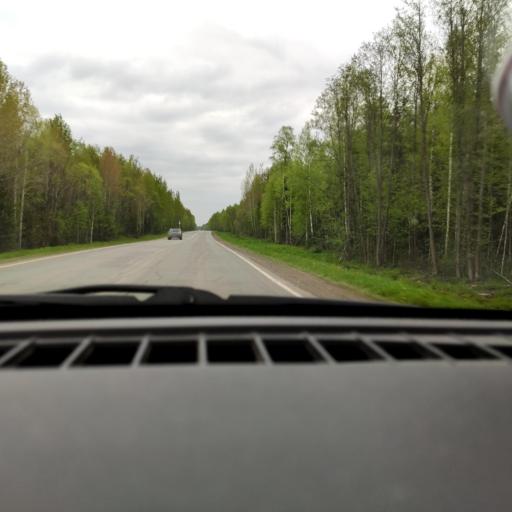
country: RU
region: Perm
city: Polazna
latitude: 58.2657
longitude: 56.1679
